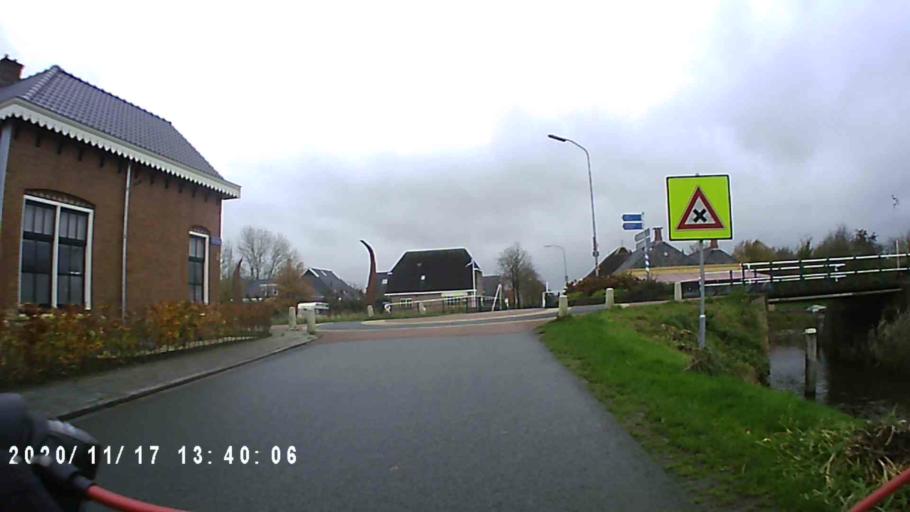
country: NL
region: Groningen
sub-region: Gemeente Zuidhorn
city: Zuidhorn
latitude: 53.2425
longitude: 6.3894
